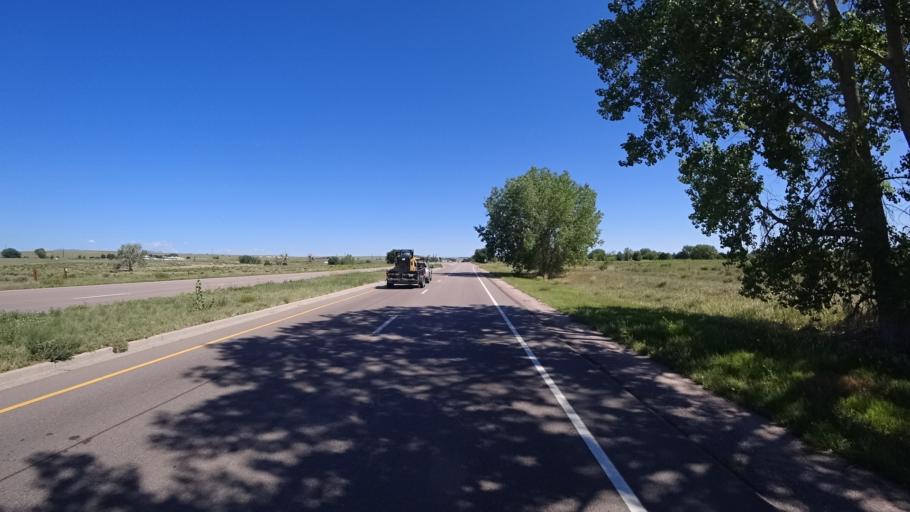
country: US
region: Colorado
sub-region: El Paso County
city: Security-Widefield
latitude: 38.7586
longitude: -104.6595
